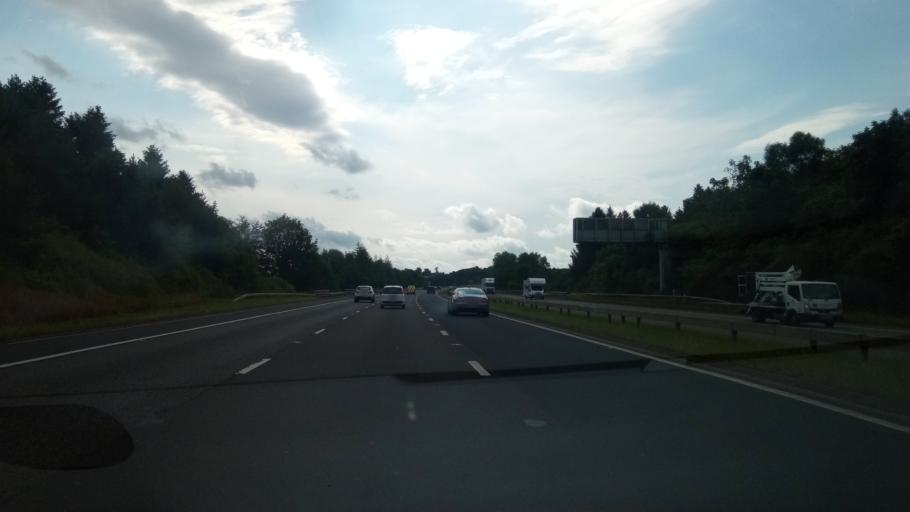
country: GB
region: England
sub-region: Cumbria
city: Penrith
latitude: 54.6439
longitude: -2.7388
